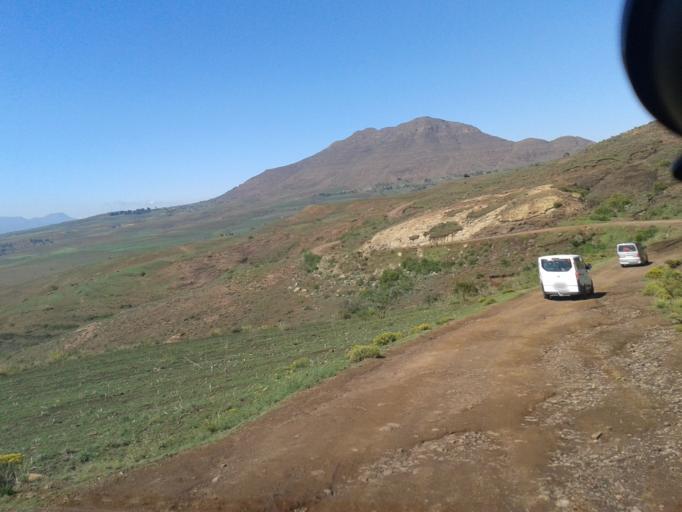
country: LS
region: Maseru
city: Nako
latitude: -29.8391
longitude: 27.5687
